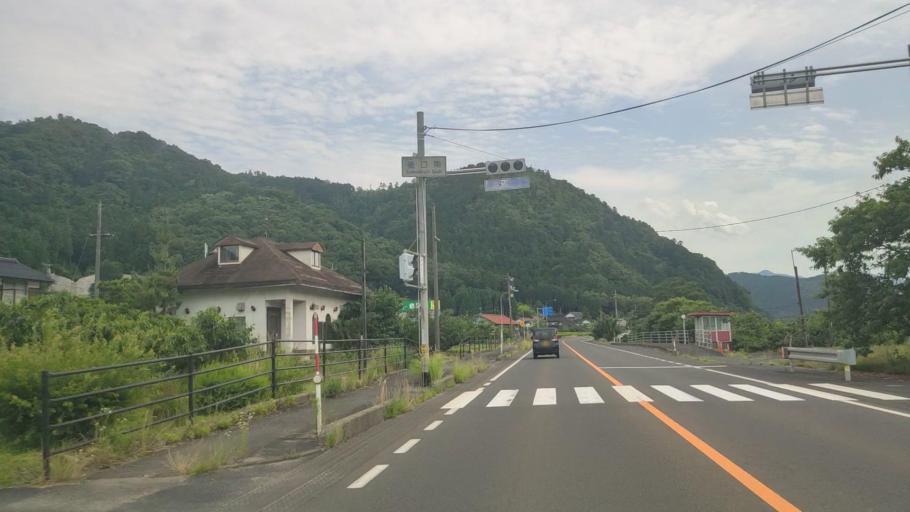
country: JP
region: Tottori
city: Tottori
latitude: 35.3703
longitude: 134.2155
